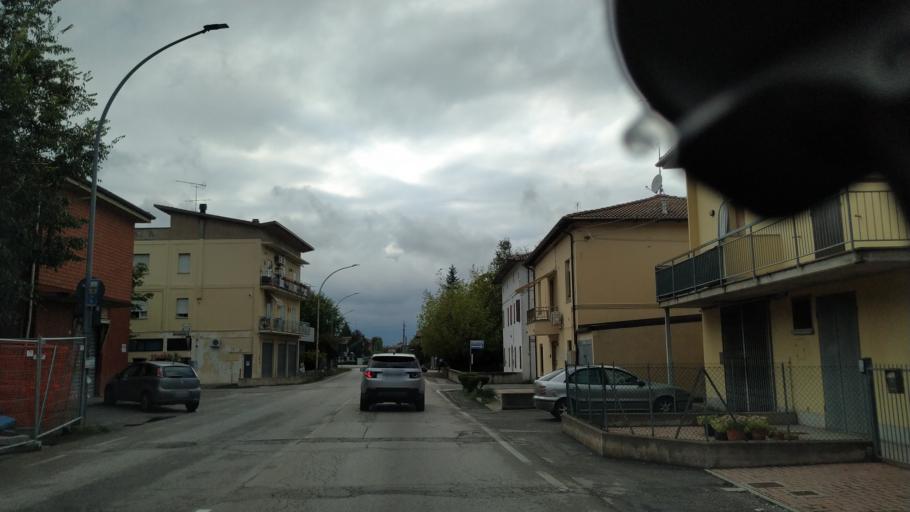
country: IT
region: Emilia-Romagna
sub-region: Provincia di Bologna
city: Decima
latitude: 44.7052
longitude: 11.2280
